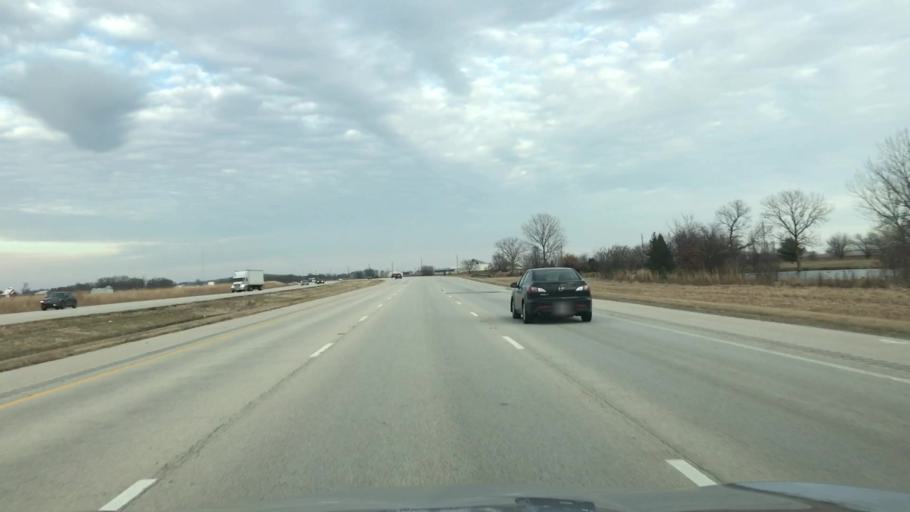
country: US
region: Illinois
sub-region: Sangamon County
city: Williamsville
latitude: 39.9681
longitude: -89.5387
